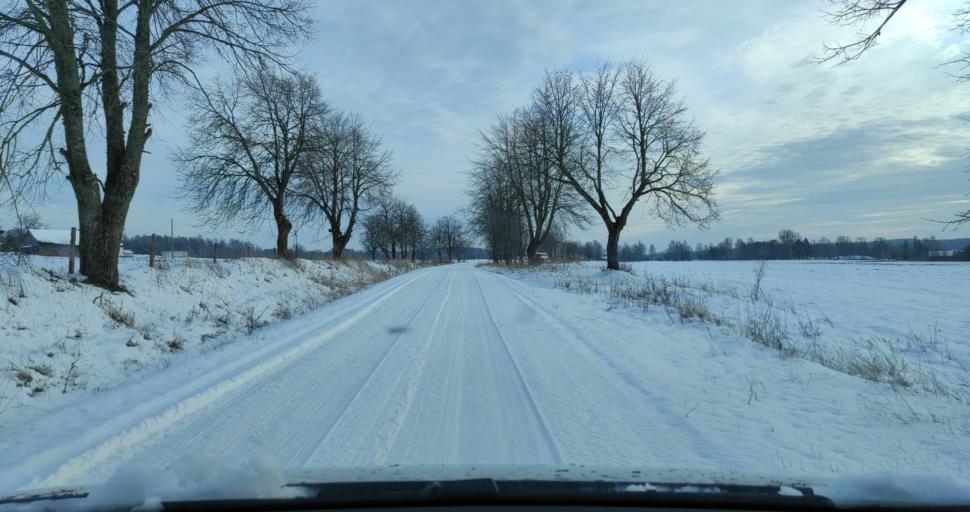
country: LV
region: Kuldigas Rajons
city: Kuldiga
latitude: 56.9474
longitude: 22.0229
